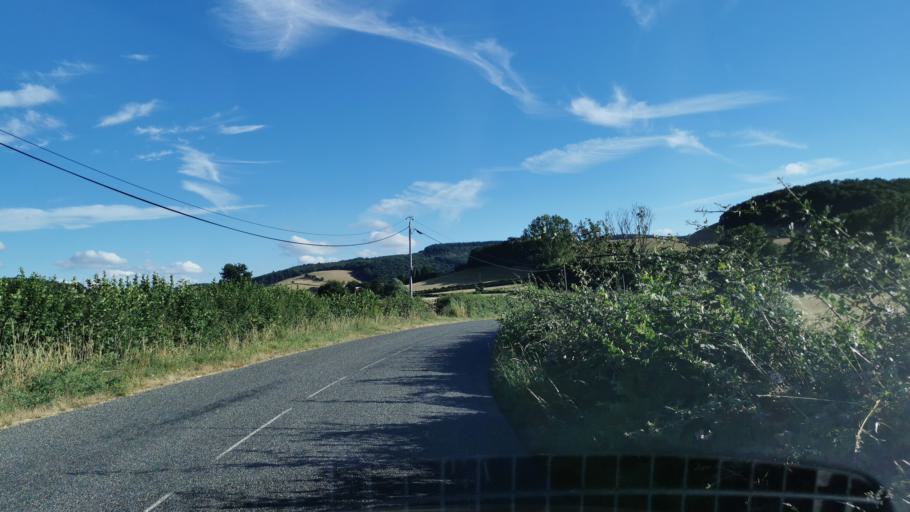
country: FR
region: Bourgogne
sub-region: Departement de Saone-et-Loire
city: Marmagne
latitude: 46.8156
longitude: 4.3287
